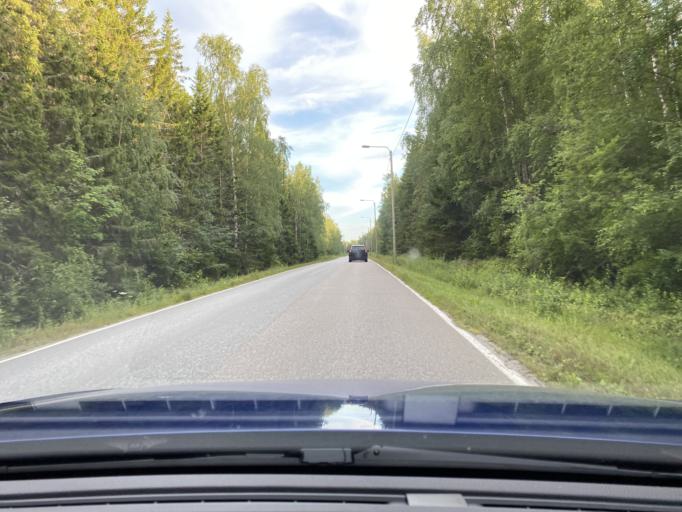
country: FI
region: Ostrobothnia
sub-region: Vaasa
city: Korsnaes
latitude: 62.9496
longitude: 21.1761
